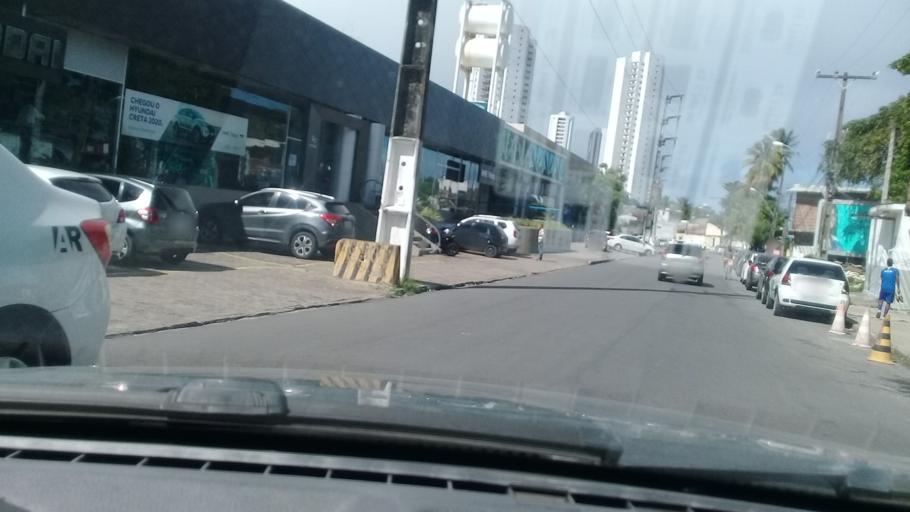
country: BR
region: Pernambuco
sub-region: Recife
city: Recife
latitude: -8.0652
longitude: -34.9080
